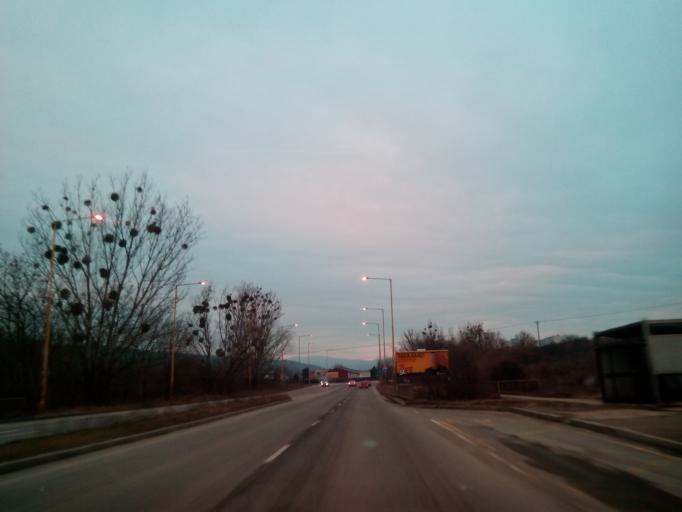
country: SK
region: Kosicky
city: Kosice
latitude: 48.7006
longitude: 21.2223
